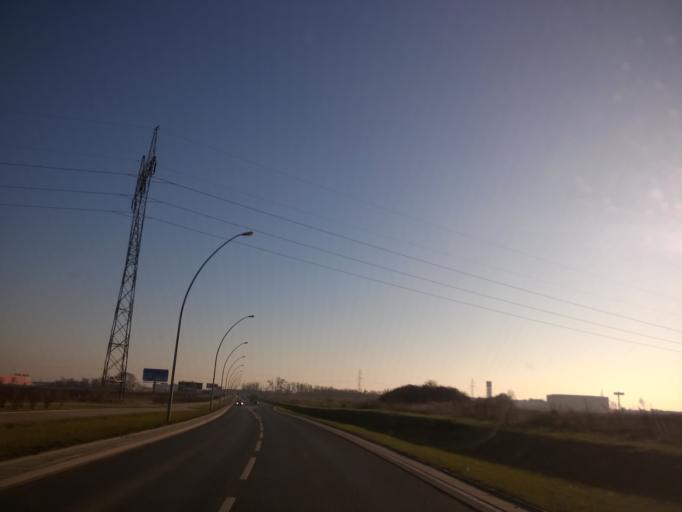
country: PL
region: Lower Silesian Voivodeship
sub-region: Powiat wroclawski
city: Bielany Wroclawskie
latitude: 51.0570
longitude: 16.9583
